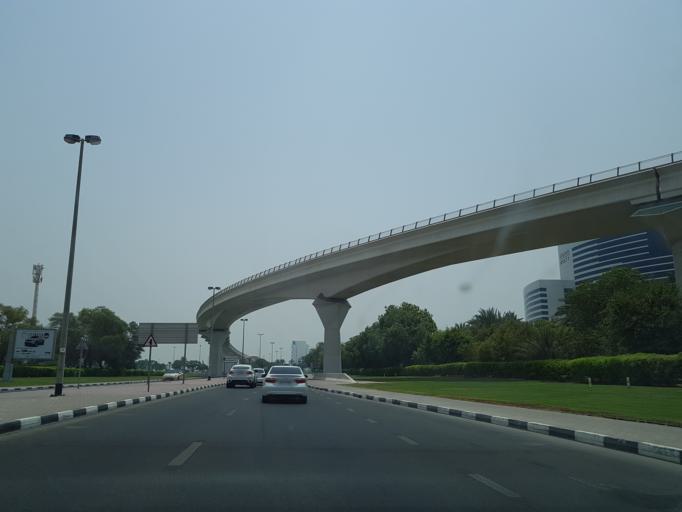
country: AE
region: Ash Shariqah
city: Sharjah
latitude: 25.2312
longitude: 55.3280
